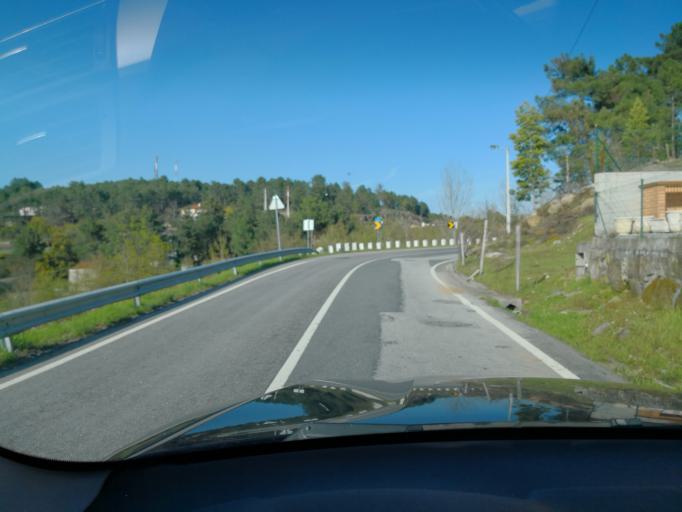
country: PT
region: Vila Real
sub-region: Vila Real
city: Vila Real
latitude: 41.3148
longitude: -7.7110
